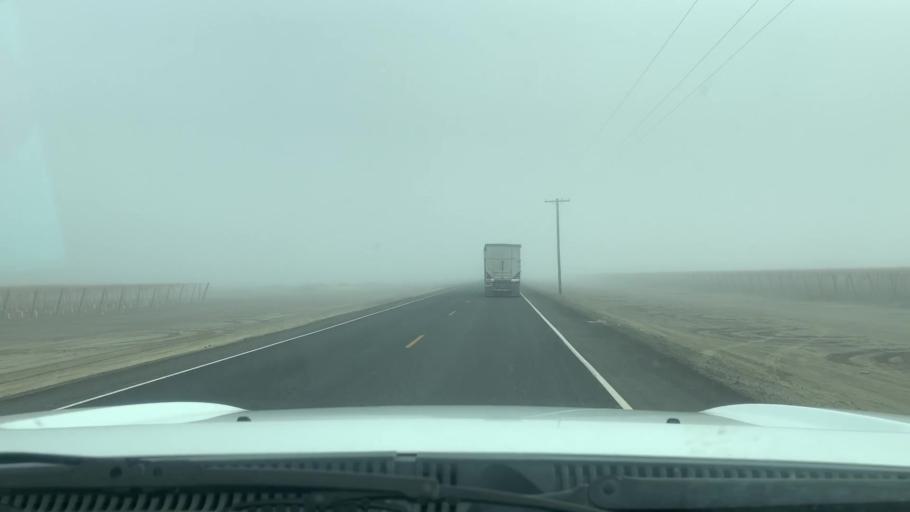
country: US
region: California
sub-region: Kern County
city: Buttonwillow
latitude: 35.4997
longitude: -119.5739
